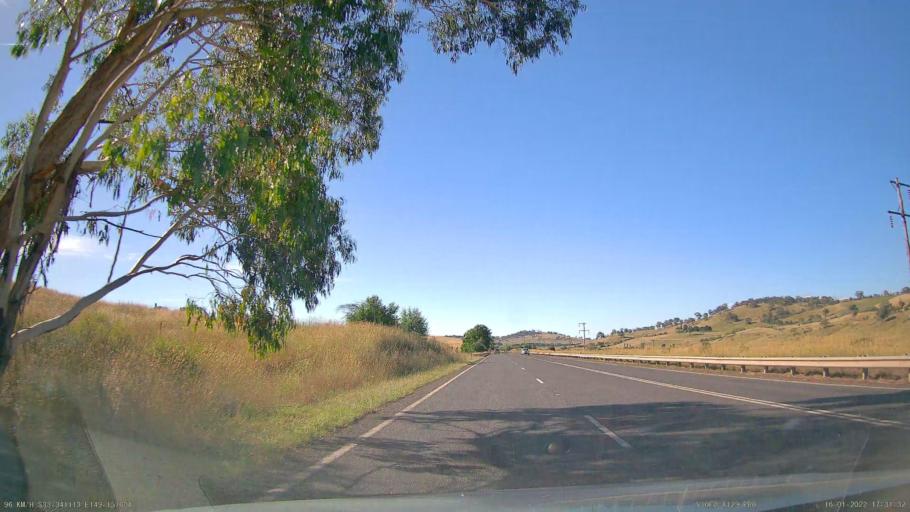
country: AU
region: New South Wales
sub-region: Orange Municipality
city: Orange
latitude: -33.3410
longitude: 149.1575
